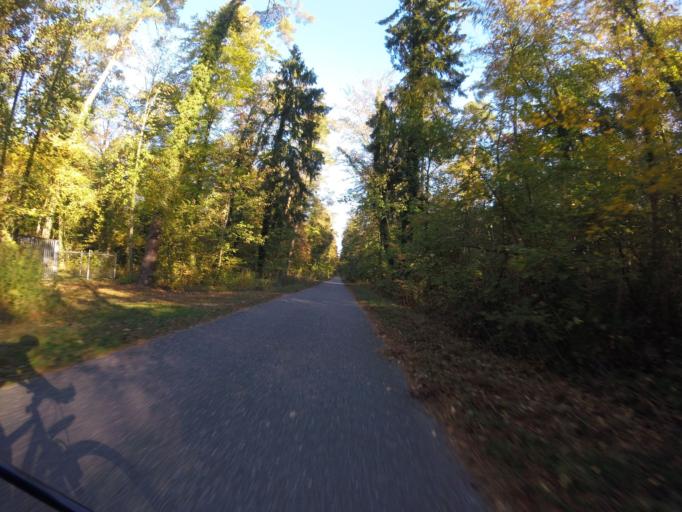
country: DE
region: Baden-Wuerttemberg
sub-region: Karlsruhe Region
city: Eggenstein-Leopoldshafen
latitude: 49.0566
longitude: 8.4089
